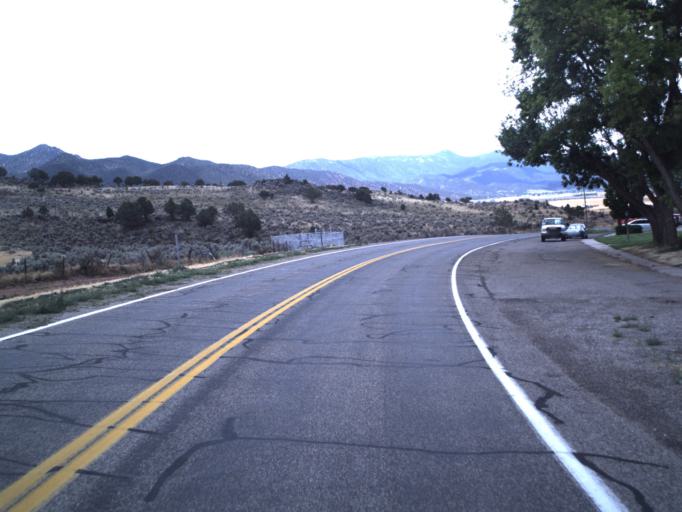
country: US
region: Utah
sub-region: Iron County
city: Parowan
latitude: 37.8823
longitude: -112.7754
